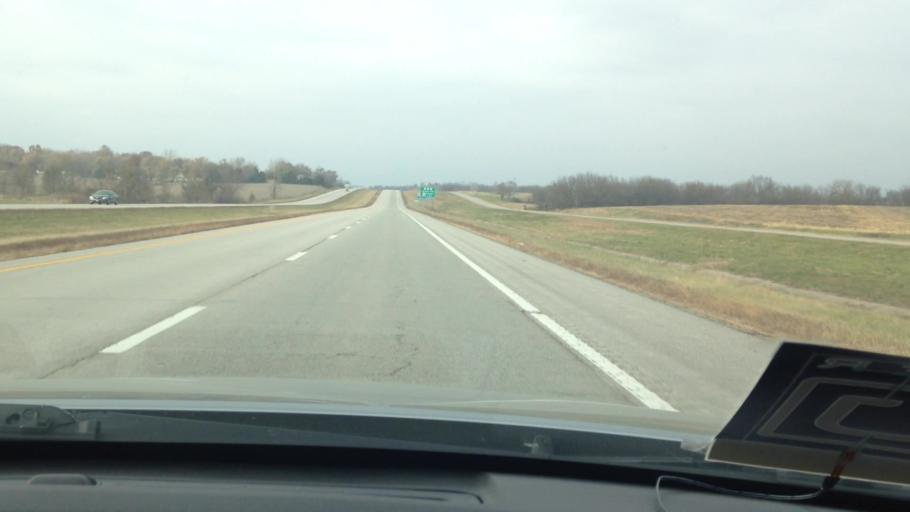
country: US
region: Missouri
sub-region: Cass County
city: Garden City
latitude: 38.5572
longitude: -94.1802
